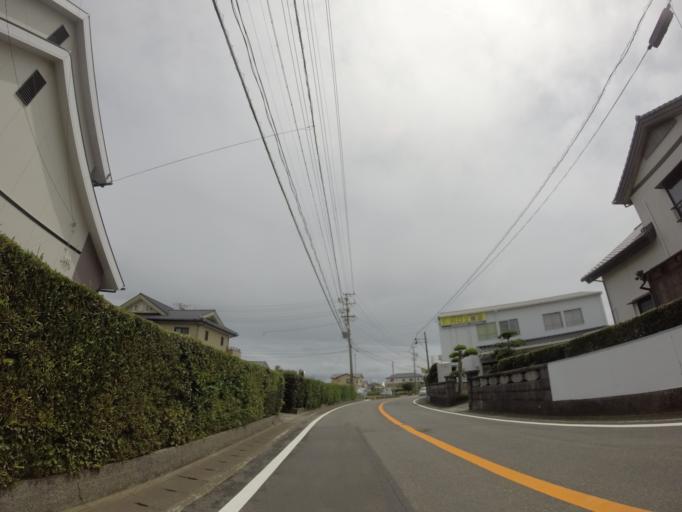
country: JP
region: Shizuoka
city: Oyama
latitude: 34.6156
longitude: 138.2020
